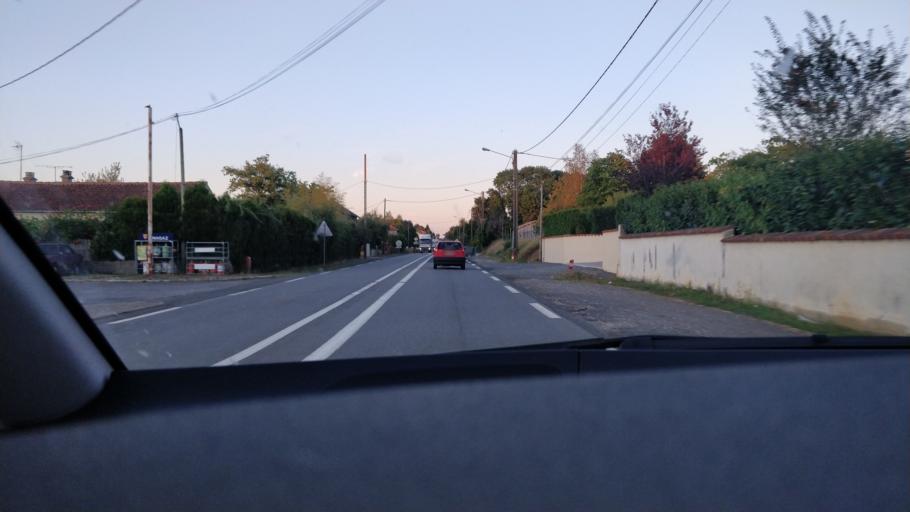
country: FR
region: Poitou-Charentes
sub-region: Departement de la Charente
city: Loubert
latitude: 45.8668
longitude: 0.5434
